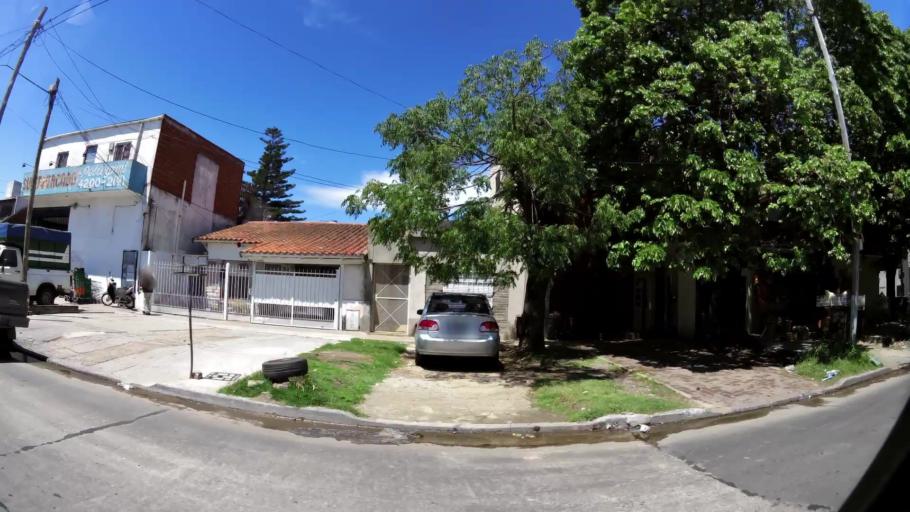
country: AR
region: Buenos Aires
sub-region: Partido de Quilmes
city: Quilmes
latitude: -34.7370
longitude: -58.2881
